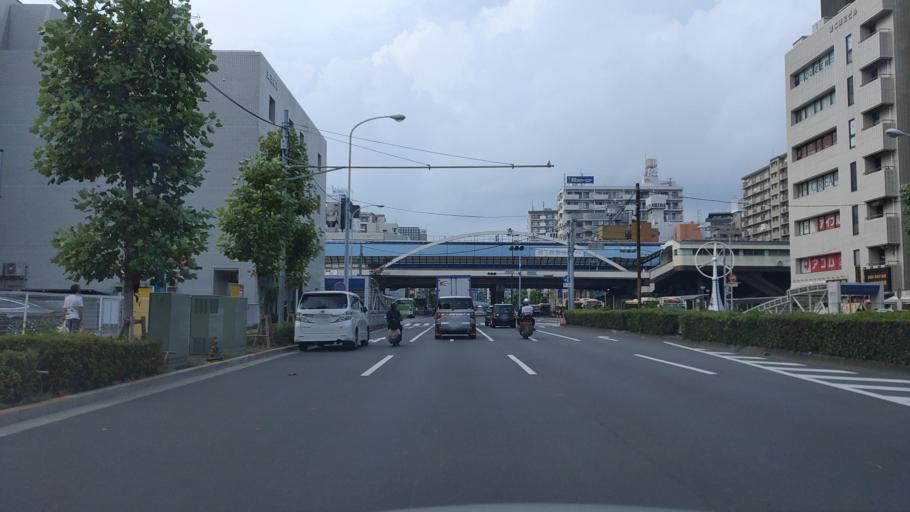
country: JP
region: Tokyo
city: Urayasu
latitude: 35.6623
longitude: 139.8730
